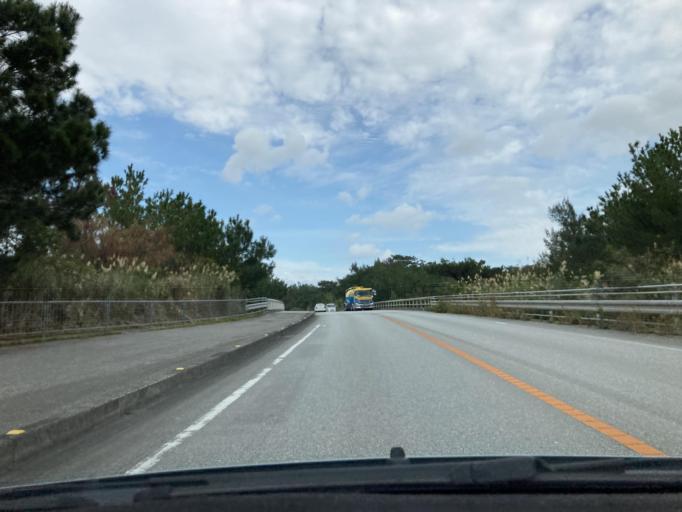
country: JP
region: Okinawa
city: Ishikawa
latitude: 26.4836
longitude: 127.8527
